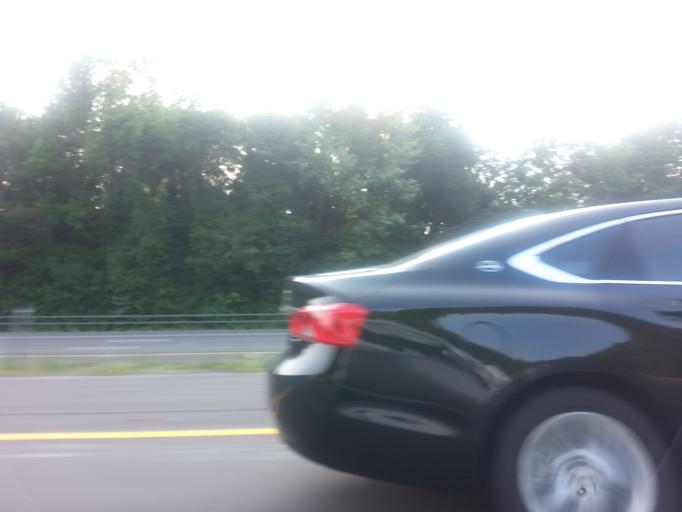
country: US
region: Tennessee
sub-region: Knox County
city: Knoxville
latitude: 35.9809
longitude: -83.9791
